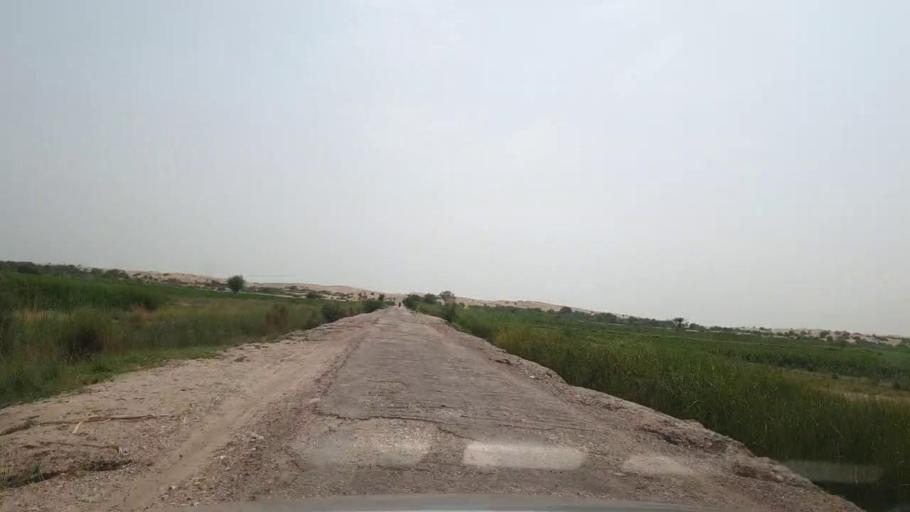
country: PK
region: Sindh
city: Rohri
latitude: 27.6181
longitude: 69.1095
